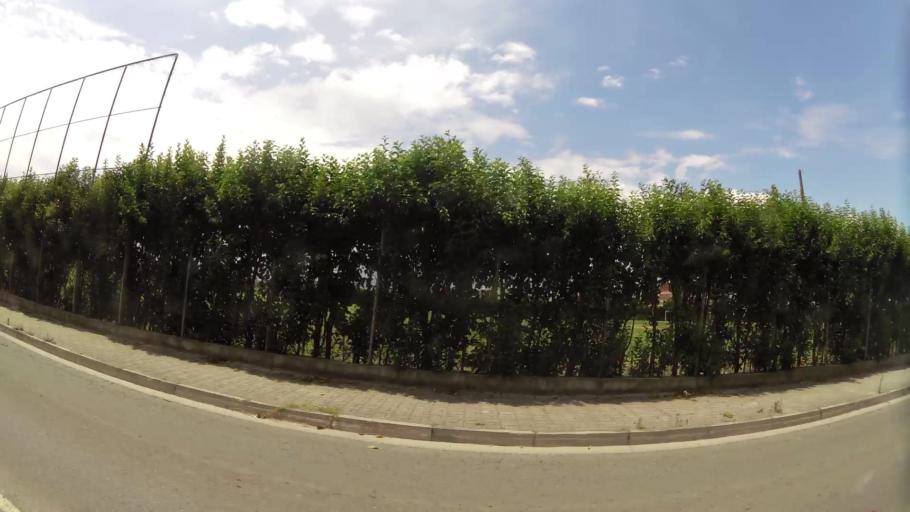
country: GR
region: Central Macedonia
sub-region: Nomos Pierias
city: Katerini
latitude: 40.2610
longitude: 22.5114
